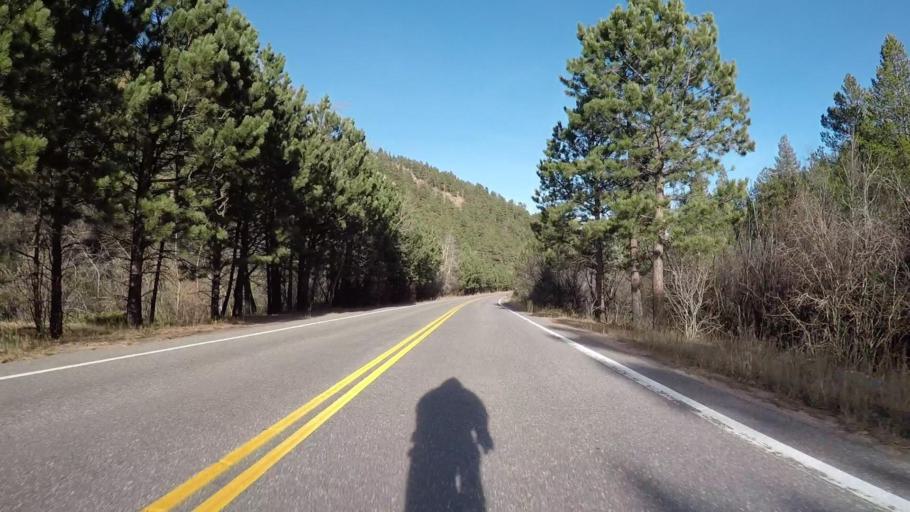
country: US
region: Colorado
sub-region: Boulder County
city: Nederland
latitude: 40.0673
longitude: -105.4477
